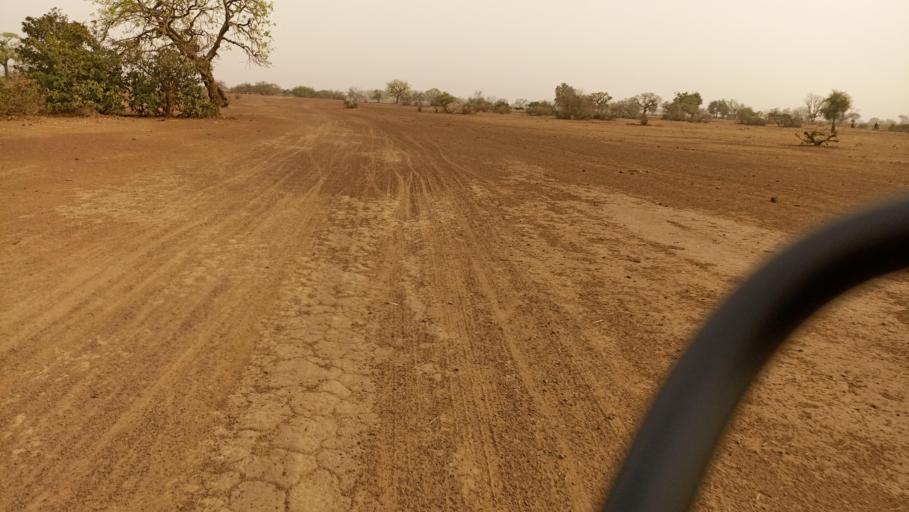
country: BF
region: Nord
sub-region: Province du Zondoma
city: Gourcy
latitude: 13.1440
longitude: -2.5973
